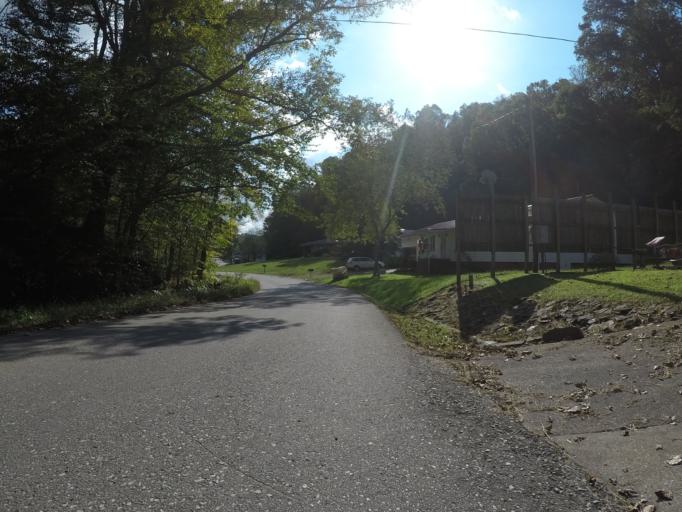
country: US
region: West Virginia
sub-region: Wayne County
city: Lavalette
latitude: 38.3530
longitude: -82.4924
